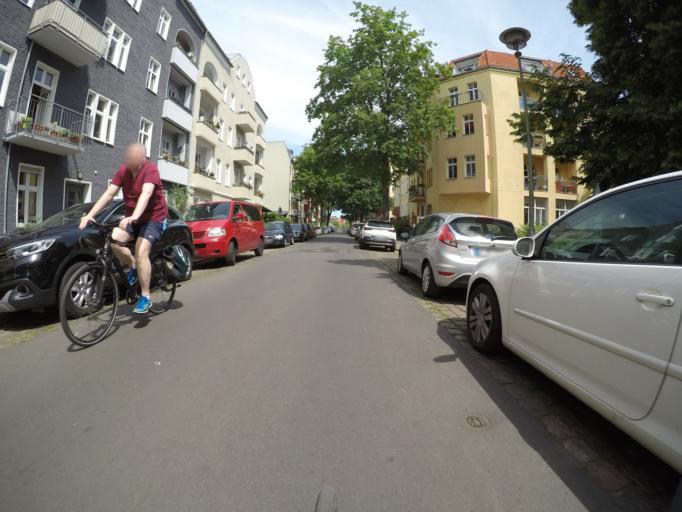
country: DE
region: Berlin
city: Kopenick Bezirk
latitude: 52.4464
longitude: 13.5704
